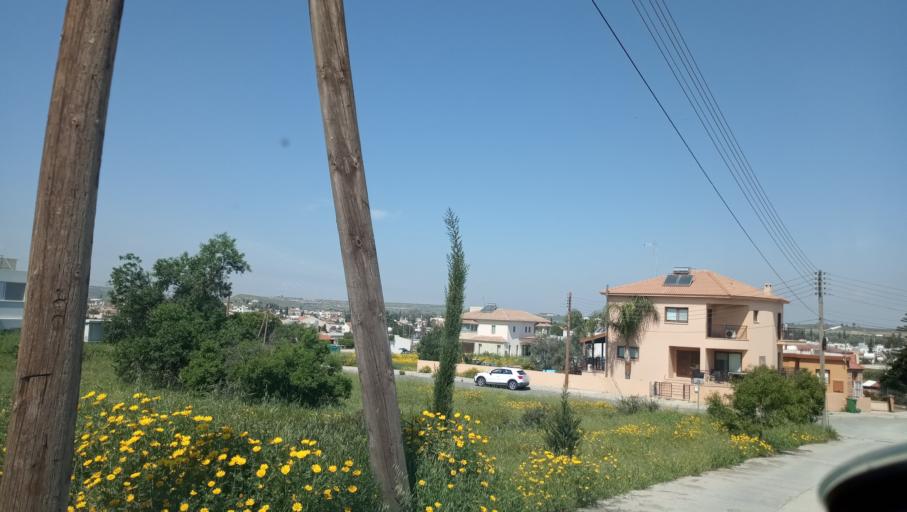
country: CY
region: Lefkosia
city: Alampra
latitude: 35.0091
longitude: 33.3973
